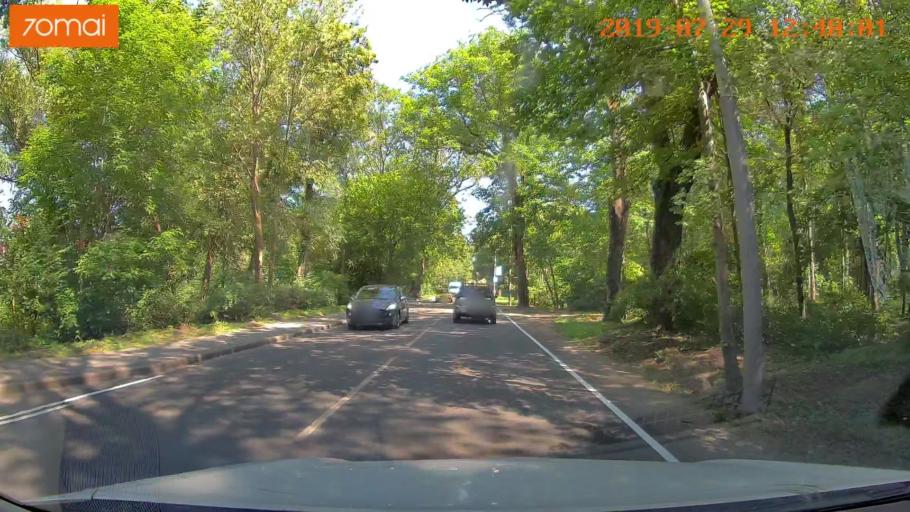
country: RU
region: Kaliningrad
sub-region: Gorod Kaliningrad
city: Kaliningrad
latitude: 54.6654
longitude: 20.5418
